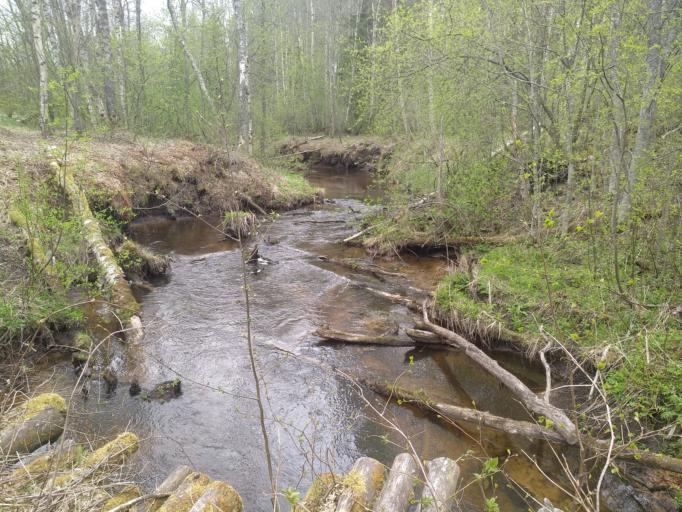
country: RU
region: Leningrad
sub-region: Vsevolzhskij Rajon
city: Vaskelovo
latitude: 60.5296
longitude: 30.4553
